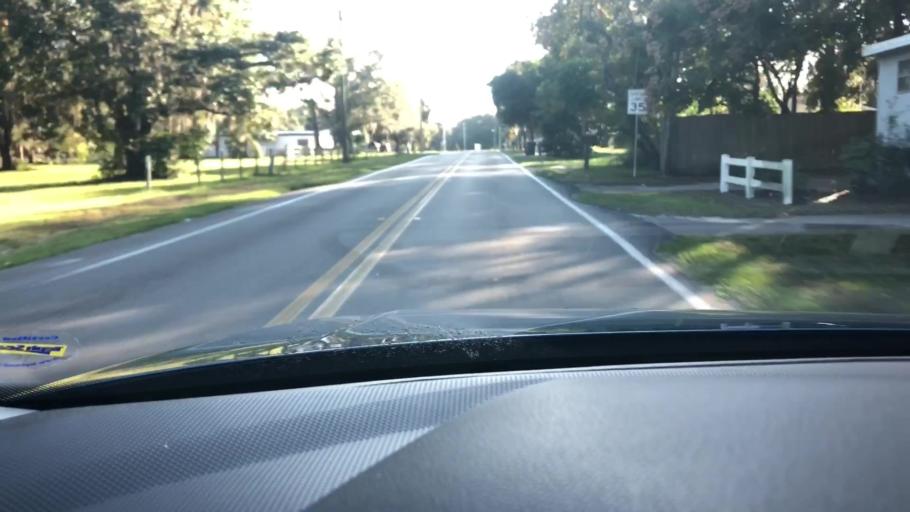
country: US
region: Florida
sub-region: Polk County
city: Kathleen
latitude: 28.1135
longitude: -82.0230
